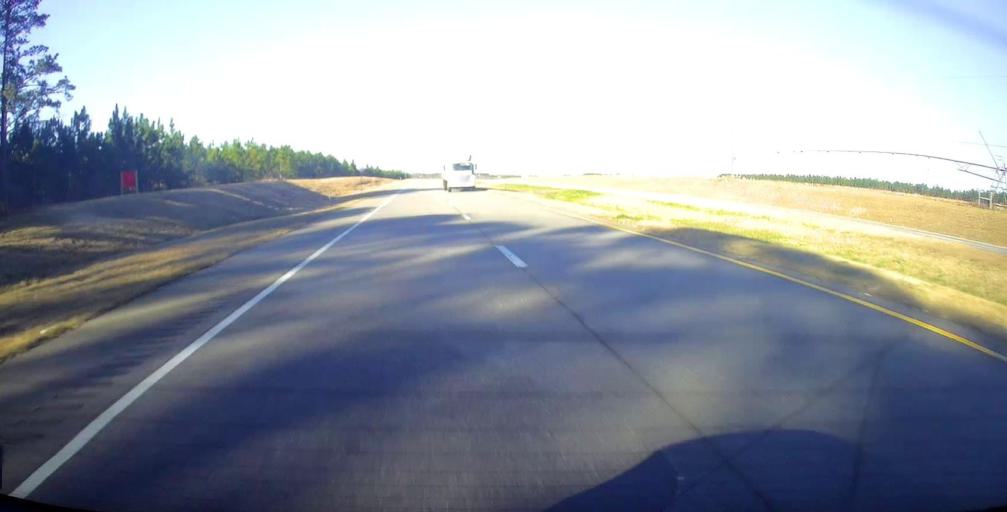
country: US
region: Georgia
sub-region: Sumter County
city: Americus
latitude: 31.9296
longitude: -84.2638
